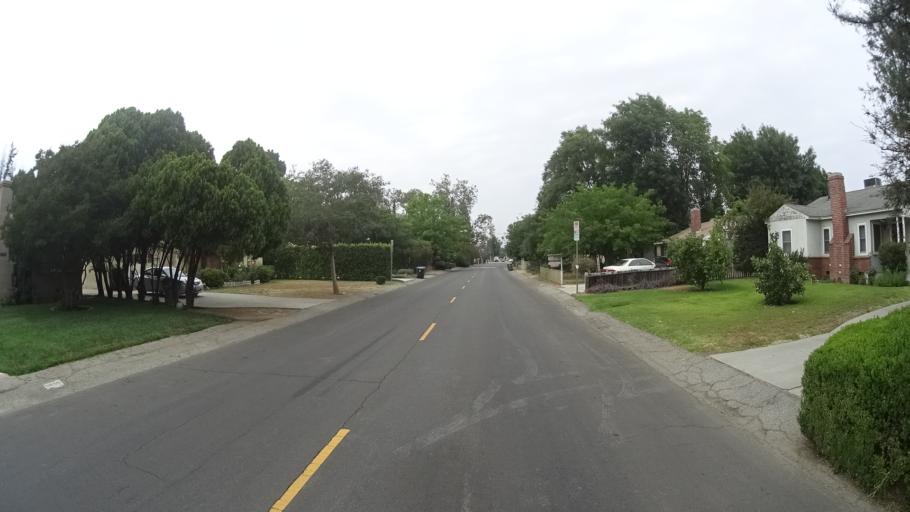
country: US
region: California
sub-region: Los Angeles County
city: Van Nuys
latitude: 34.1775
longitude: -118.4510
